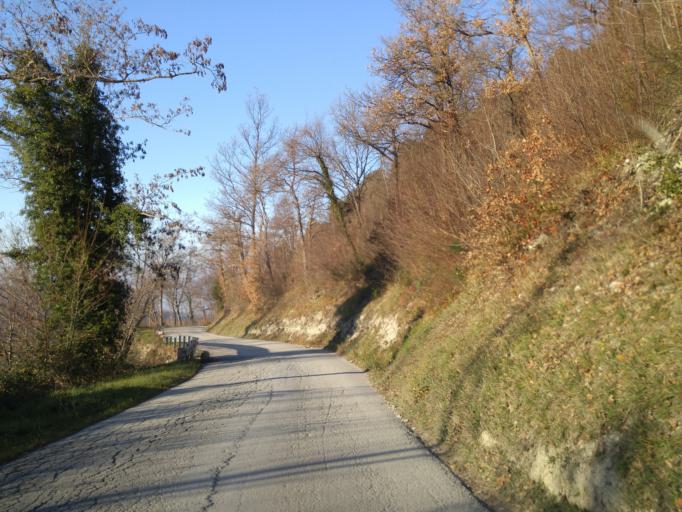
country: IT
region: The Marches
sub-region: Provincia di Pesaro e Urbino
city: Isola del Piano
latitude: 43.7236
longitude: 12.7486
